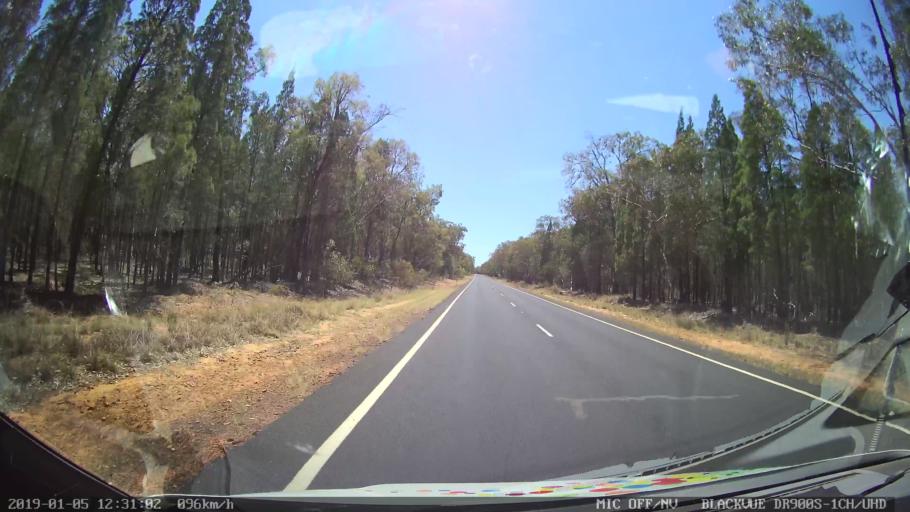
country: AU
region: New South Wales
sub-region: Warrumbungle Shire
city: Coonabarabran
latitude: -31.2240
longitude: 149.3591
